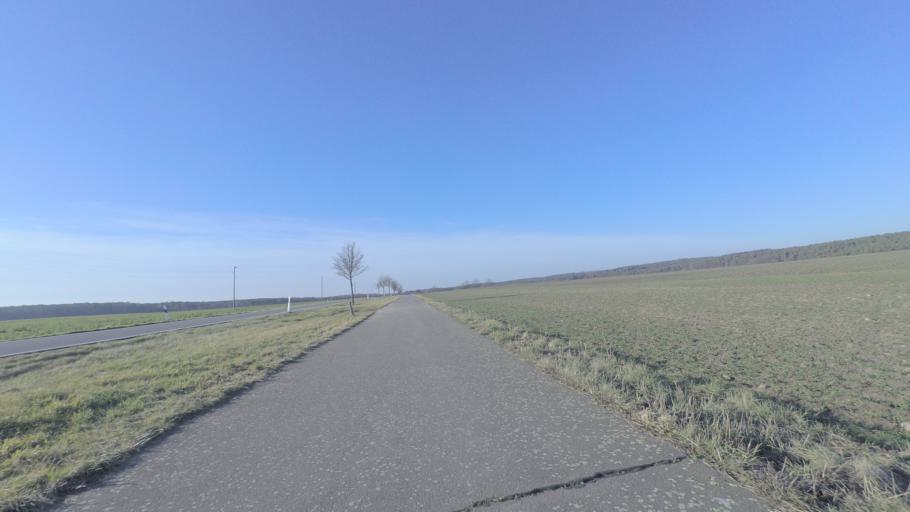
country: DE
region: Brandenburg
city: Ihlow
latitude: 51.9927
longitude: 13.3544
